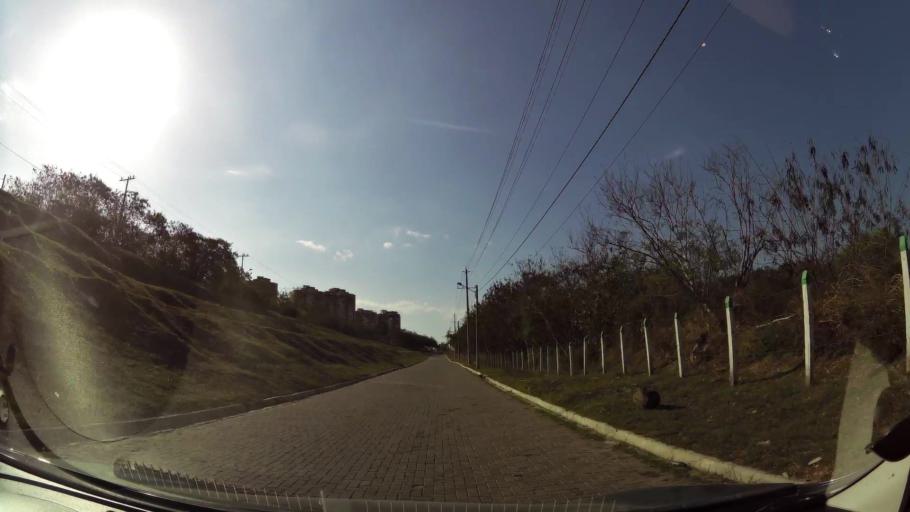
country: CO
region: Atlantico
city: Barranquilla
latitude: 11.0029
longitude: -74.8378
